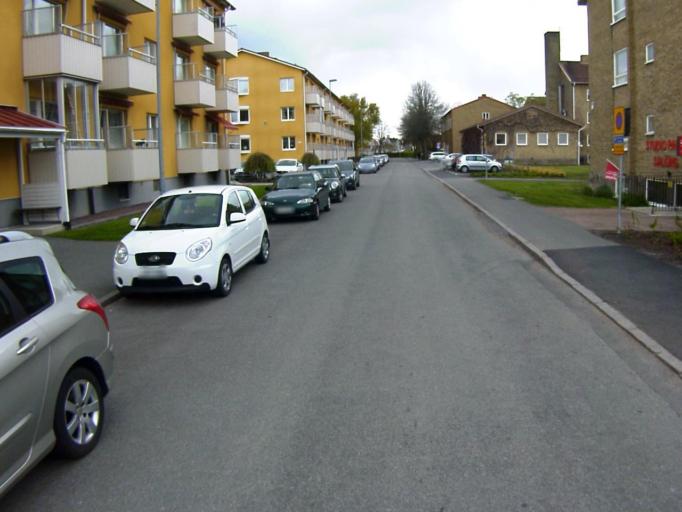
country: SE
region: Skane
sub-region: Kristianstads Kommun
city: Kristianstad
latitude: 56.0408
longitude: 14.1645
